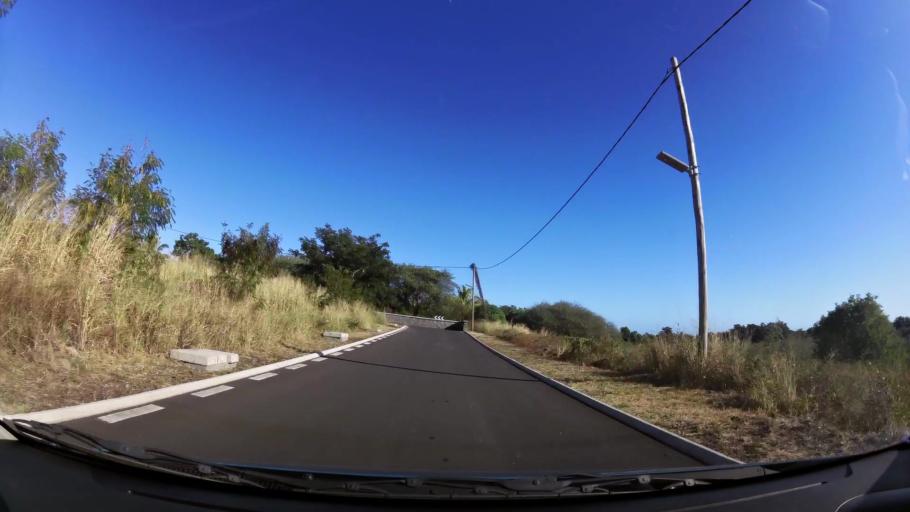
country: MU
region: Black River
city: Tamarin
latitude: -20.3353
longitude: 57.3826
